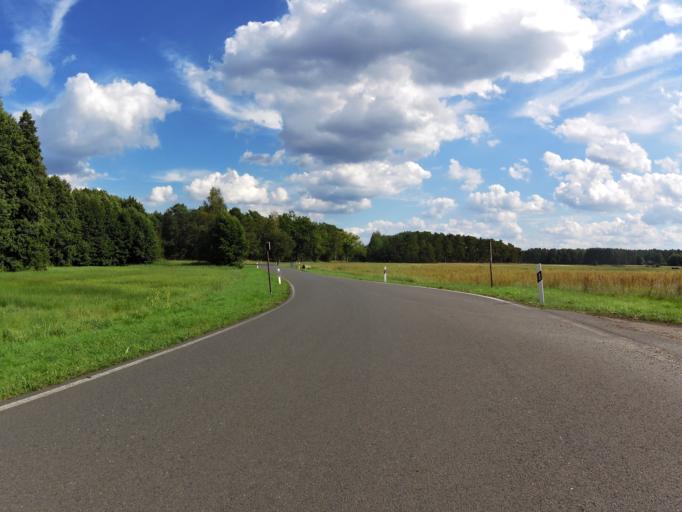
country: DE
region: Brandenburg
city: Munchehofe
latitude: 52.1983
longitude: 13.8600
